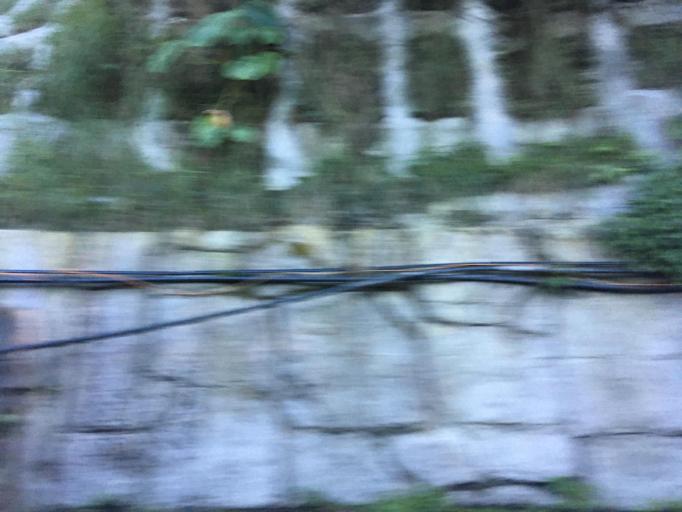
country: TW
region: Taiwan
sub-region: Yilan
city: Yilan
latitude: 24.5382
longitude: 121.5117
